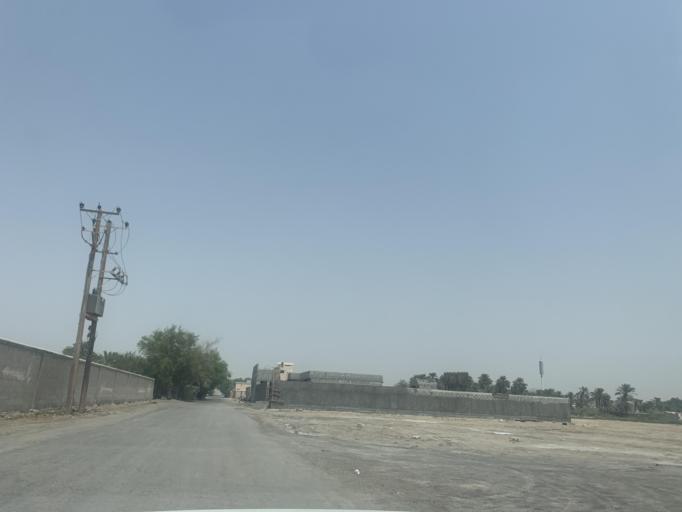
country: BH
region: Central Governorate
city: Madinat Hamad
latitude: 26.1237
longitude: 50.4688
